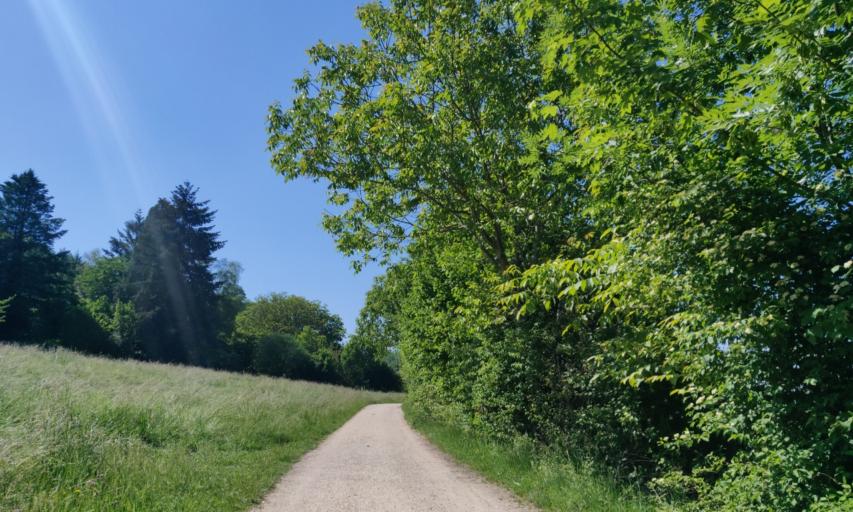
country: CH
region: Basel-Landschaft
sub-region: Bezirk Arlesheim
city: Pfeffingen
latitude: 47.4694
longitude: 7.5839
